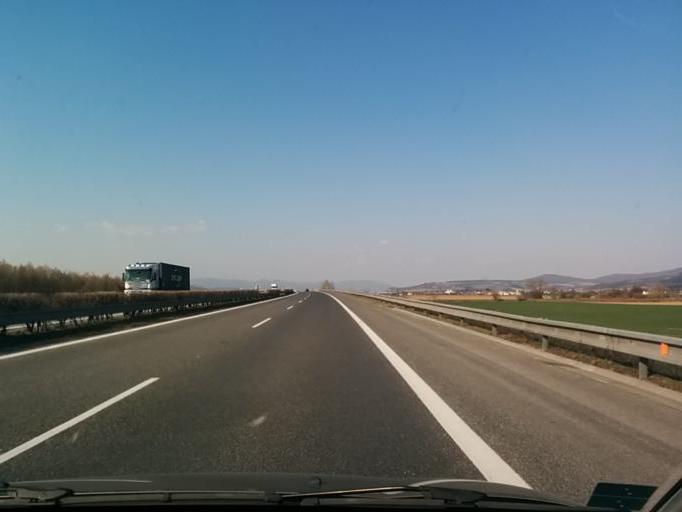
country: SK
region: Trenciansky
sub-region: Okres Nove Mesto nad Vahom
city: Nove Mesto nad Vahom
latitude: 48.7165
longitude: 17.8743
